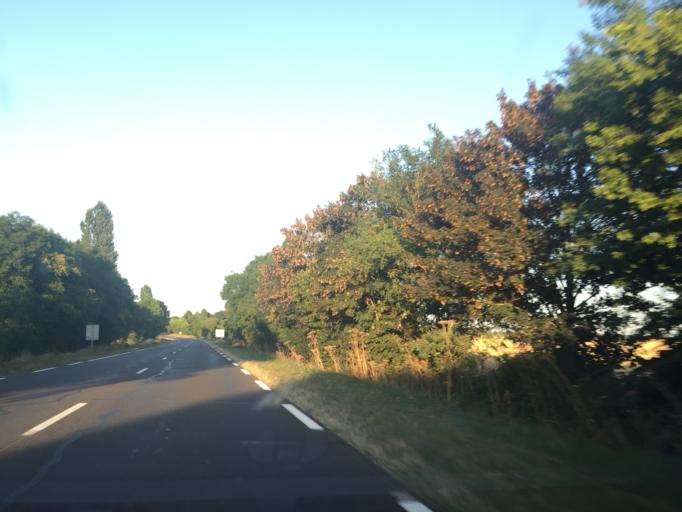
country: FR
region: Poitou-Charentes
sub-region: Departement de la Vienne
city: Lusignan
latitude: 46.4267
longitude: 0.1204
